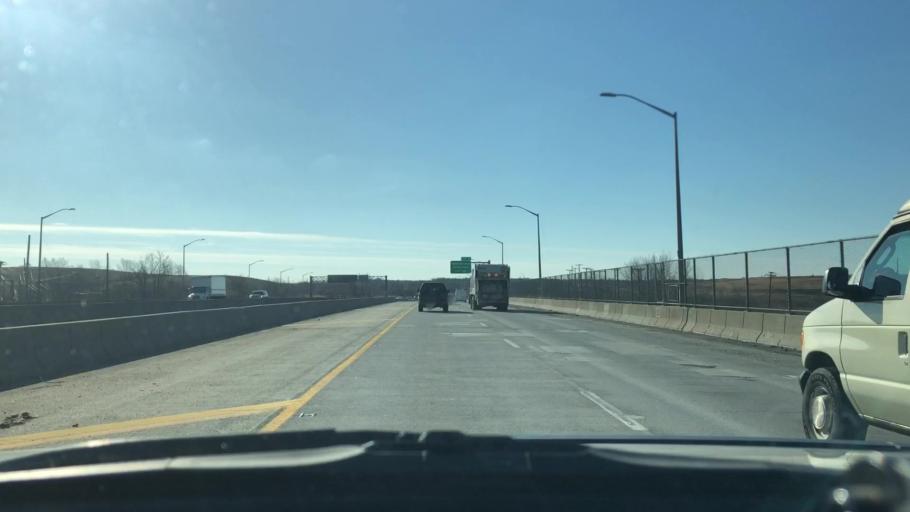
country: US
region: New York
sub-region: Richmond County
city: Bloomfield
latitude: 40.5774
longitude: -74.1908
